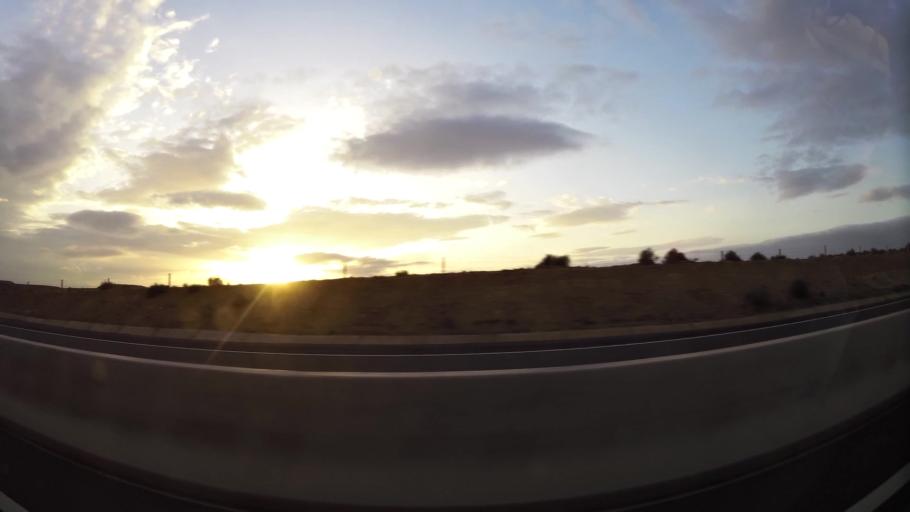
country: MA
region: Oriental
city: Taourirt
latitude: 34.5056
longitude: -2.9500
